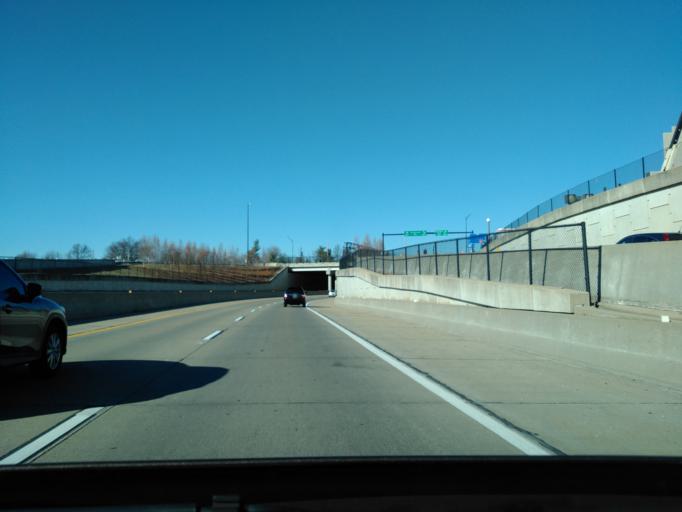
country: US
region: Missouri
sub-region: Saint Louis County
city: Valley Park
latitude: 38.5662
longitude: -90.4993
